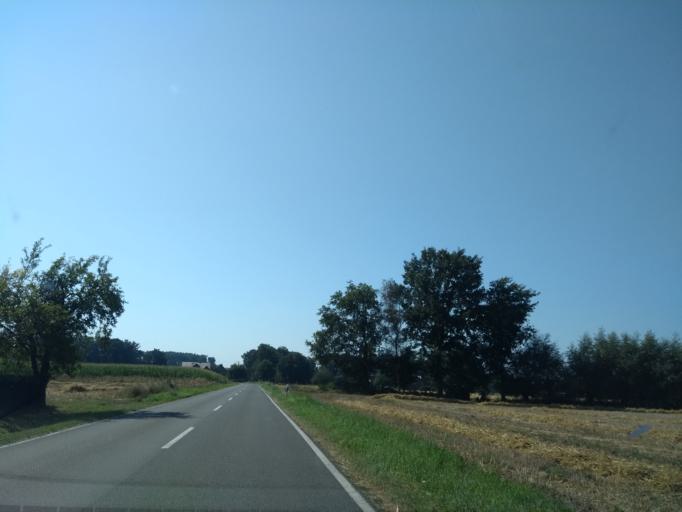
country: DE
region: North Rhine-Westphalia
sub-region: Regierungsbezirk Arnsberg
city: Lippstadt
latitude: 51.7260
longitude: 8.3884
